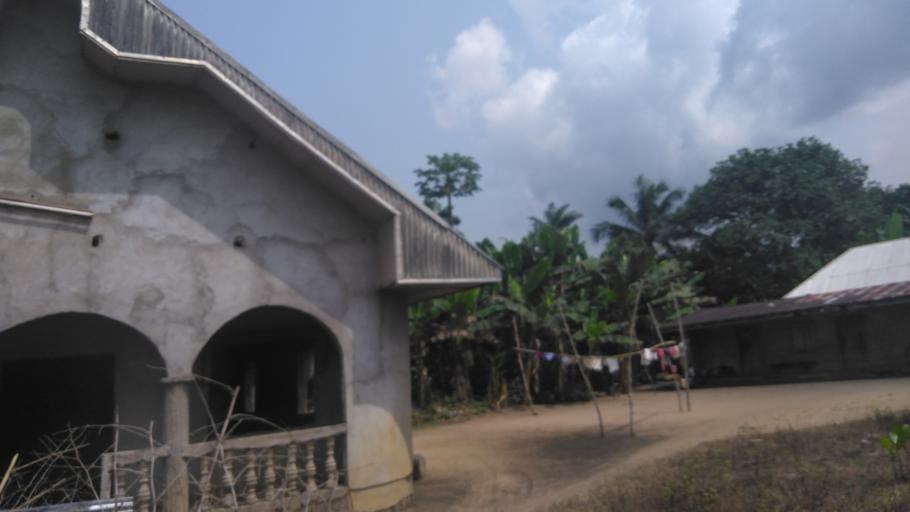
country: NG
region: Abia
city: Aba
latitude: 5.0477
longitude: 7.2397
